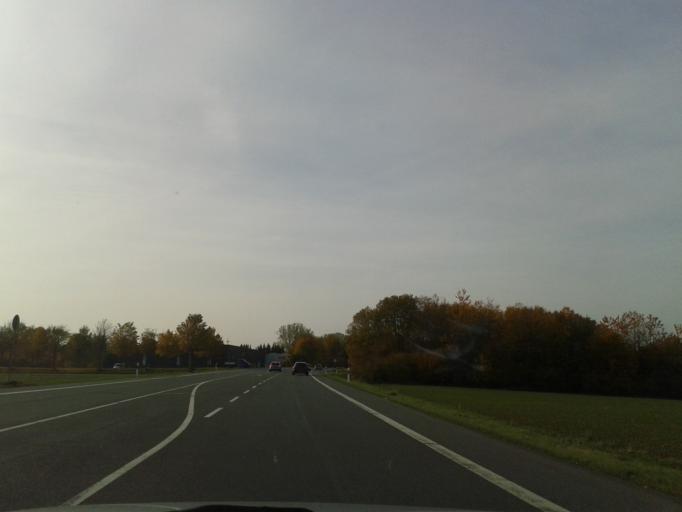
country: DE
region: North Rhine-Westphalia
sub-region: Regierungsbezirk Arnsberg
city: Ruthen
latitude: 51.5284
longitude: 8.4624
